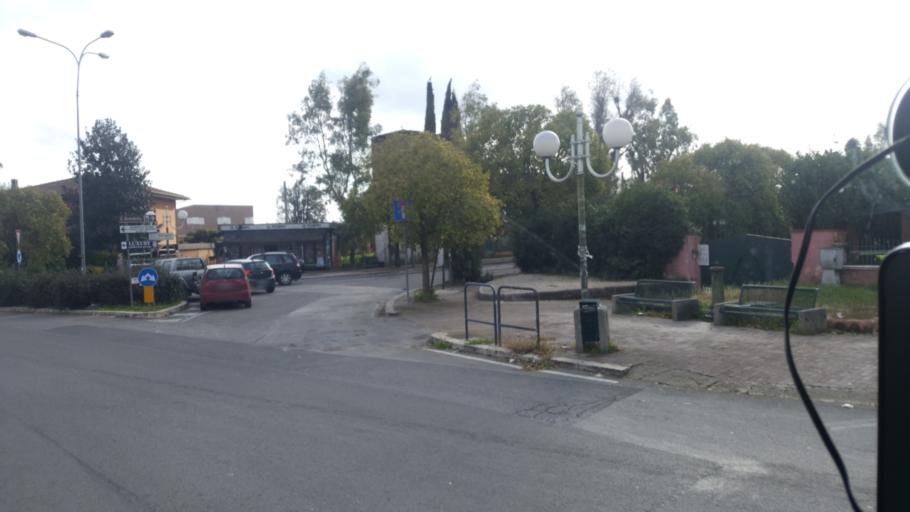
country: IT
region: Latium
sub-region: Provincia di Latina
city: Borgo Podgora
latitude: 41.4818
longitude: 12.8636
